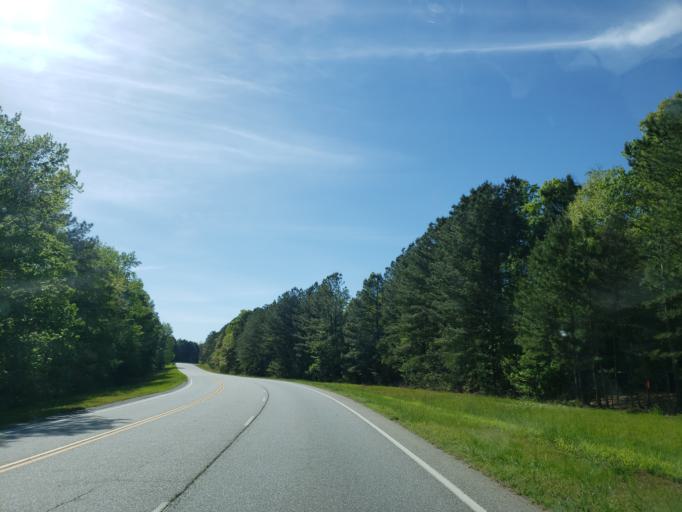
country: US
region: Georgia
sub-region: Haralson County
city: Tallapoosa
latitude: 33.7142
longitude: -85.2734
